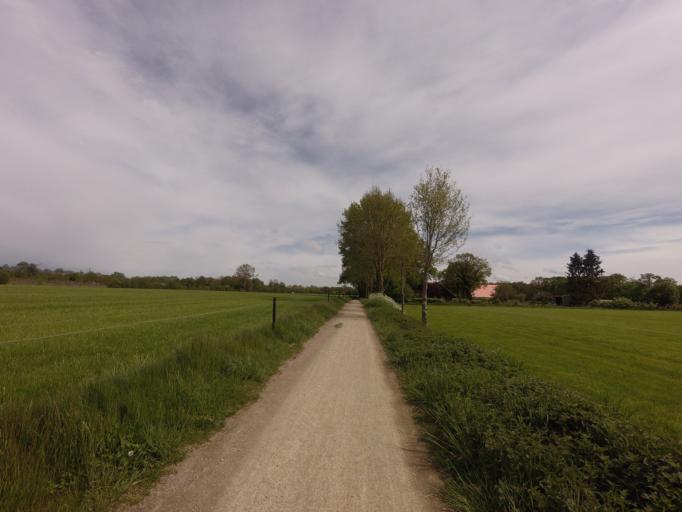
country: NL
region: Overijssel
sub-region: Gemeente Hengelo
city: Hengelo
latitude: 52.2362
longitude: 6.7551
